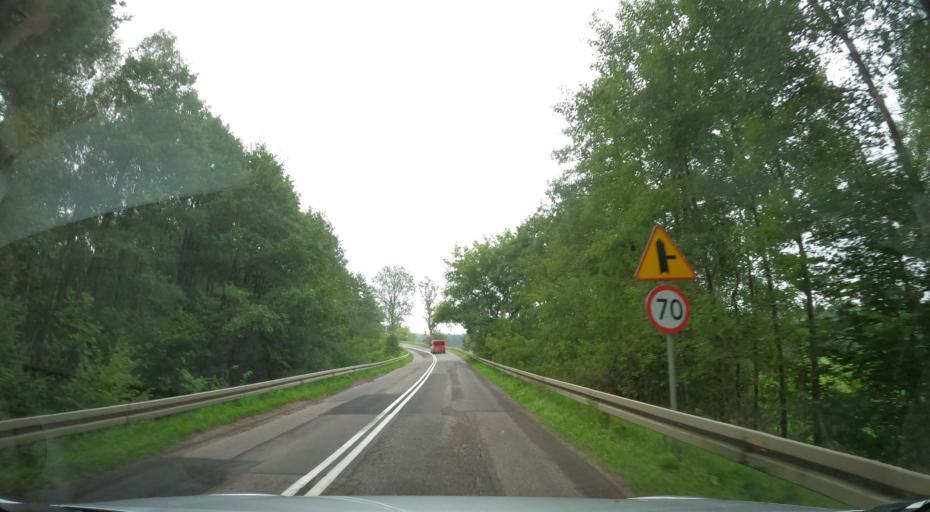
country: PL
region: Pomeranian Voivodeship
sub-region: Powiat wejherowski
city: Linia
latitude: 54.4584
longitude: 18.0018
